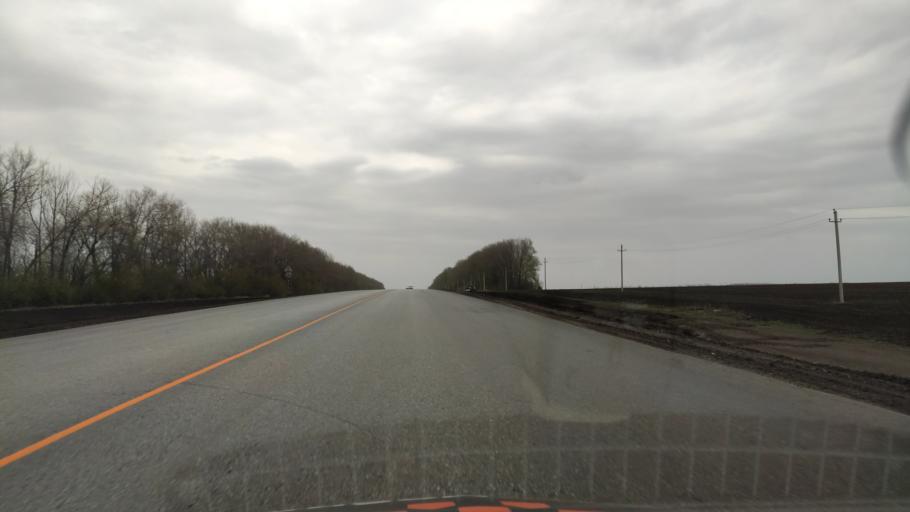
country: RU
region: Kursk
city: Gorshechnoye
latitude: 51.5474
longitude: 38.0696
